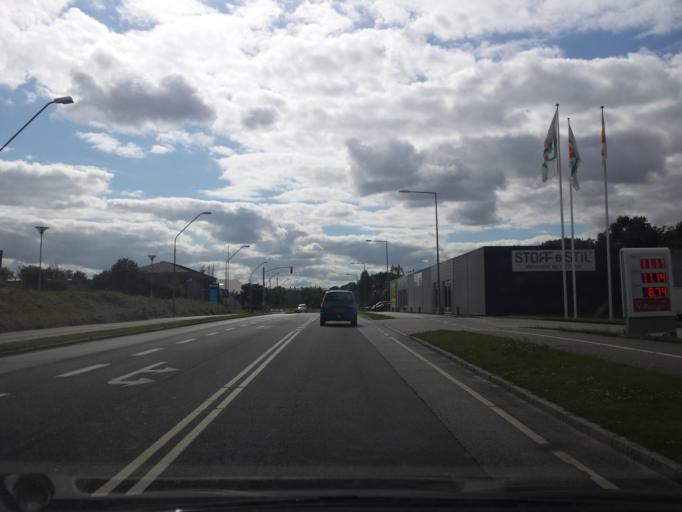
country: DK
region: South Denmark
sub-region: Sonderborg Kommune
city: Sonderborg
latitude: 54.9239
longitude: 9.8068
